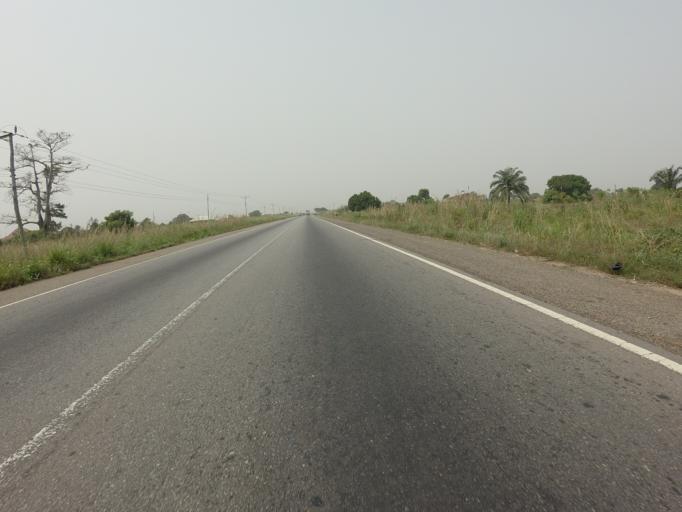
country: GH
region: Volta
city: Anloga
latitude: 5.8901
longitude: 0.4739
